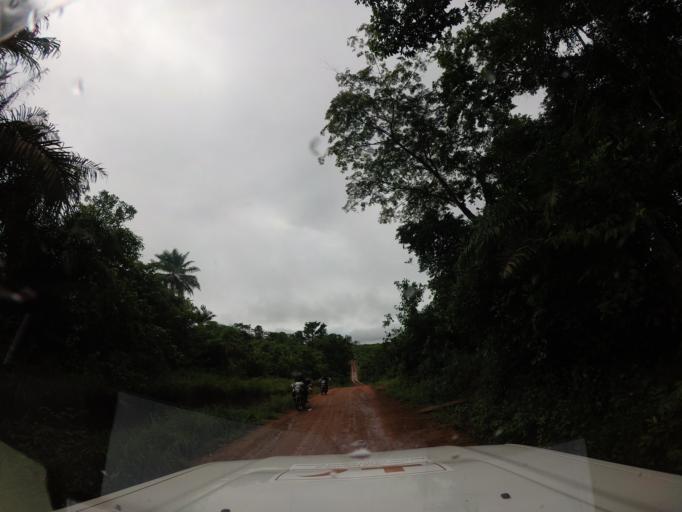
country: SL
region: Eastern Province
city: Kenema
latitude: 7.7084
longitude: -11.1830
